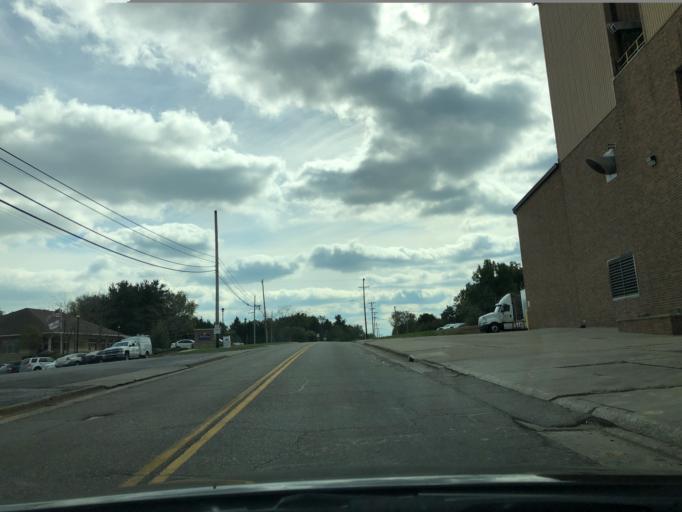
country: US
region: Ohio
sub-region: Stark County
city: Brewster
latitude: 40.7065
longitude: -81.5981
